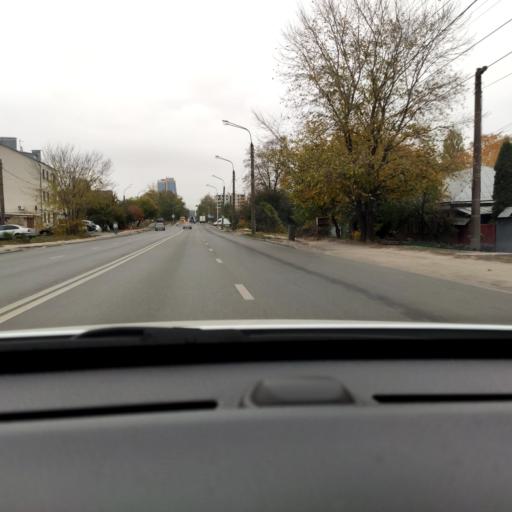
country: RU
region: Voronezj
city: Voronezh
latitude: 51.6948
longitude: 39.1725
